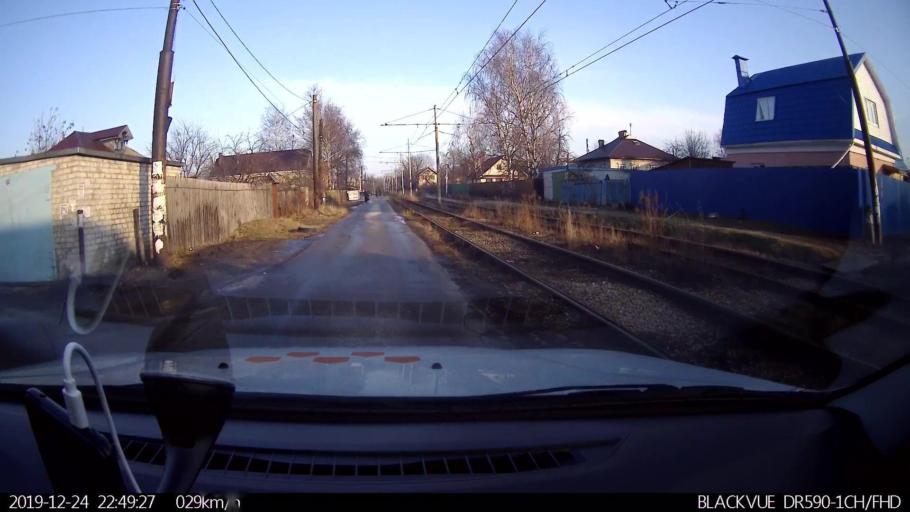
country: RU
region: Nizjnij Novgorod
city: Nizhniy Novgorod
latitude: 56.2871
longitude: 43.8982
